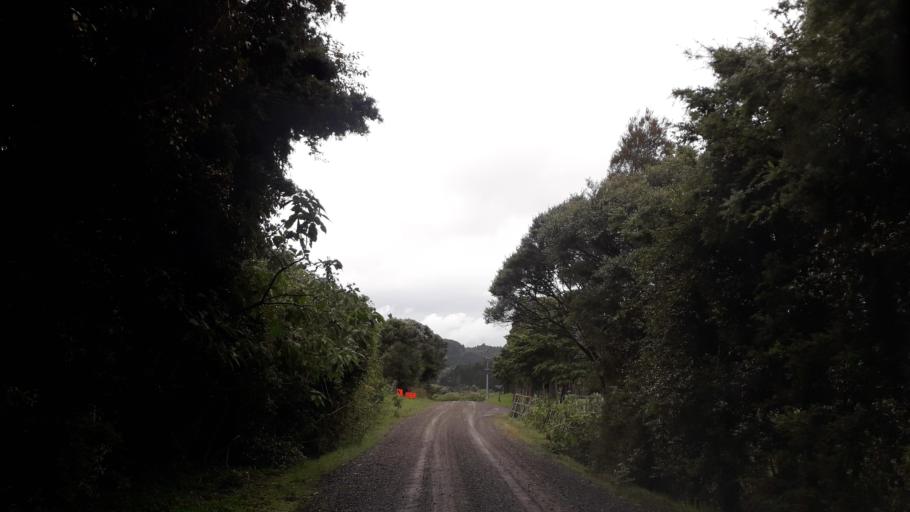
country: NZ
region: Northland
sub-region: Far North District
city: Kaitaia
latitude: -35.3892
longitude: 173.4046
